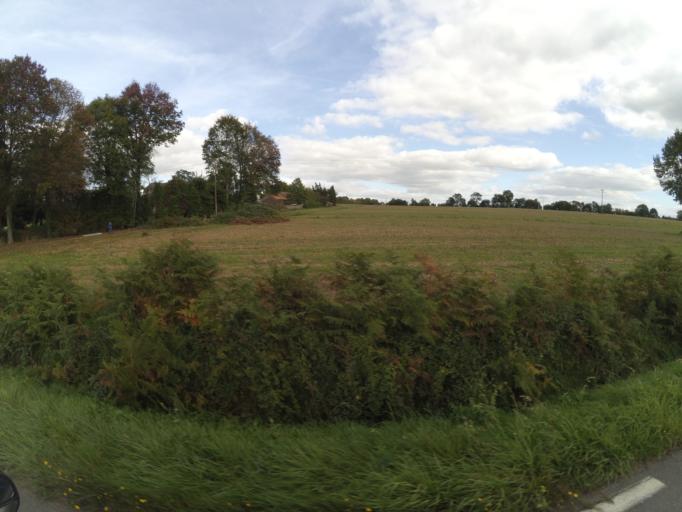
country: FR
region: Pays de la Loire
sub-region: Departement de la Loire-Atlantique
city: Carquefou
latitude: 47.3165
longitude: -1.5094
